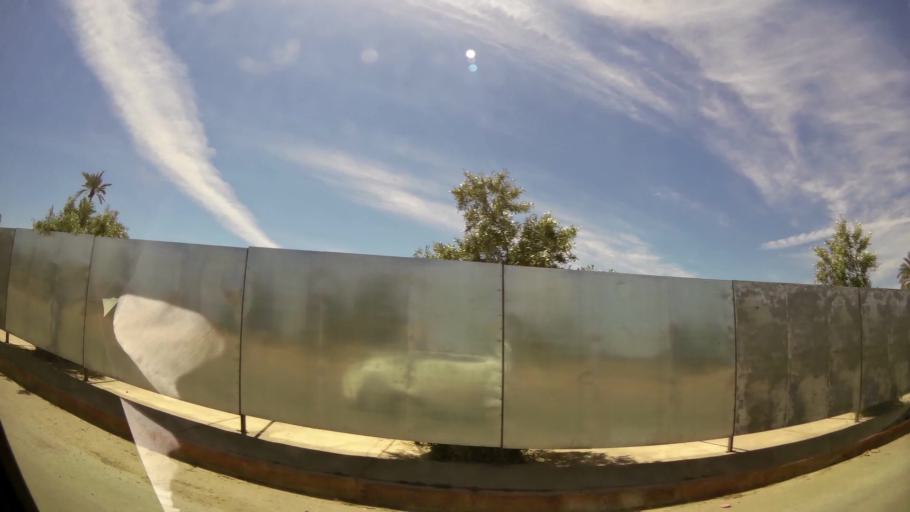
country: MA
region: Marrakech-Tensift-Al Haouz
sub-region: Marrakech
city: Marrakesh
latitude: 31.6710
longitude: -7.9980
